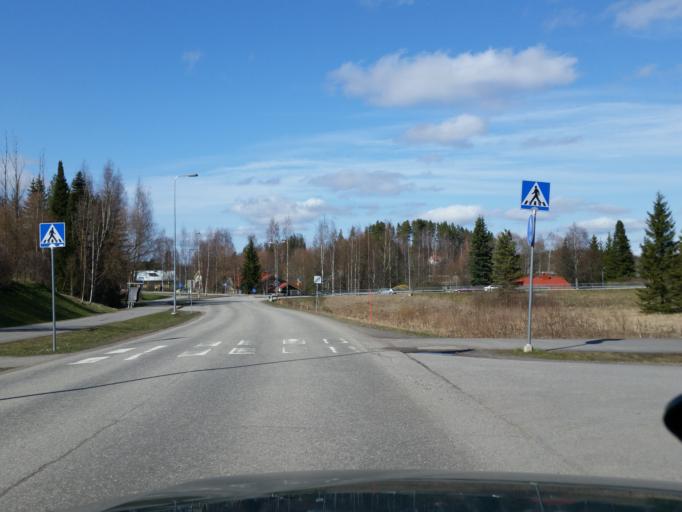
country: FI
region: Uusimaa
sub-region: Helsinki
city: Vihti
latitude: 60.4123
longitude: 24.3304
